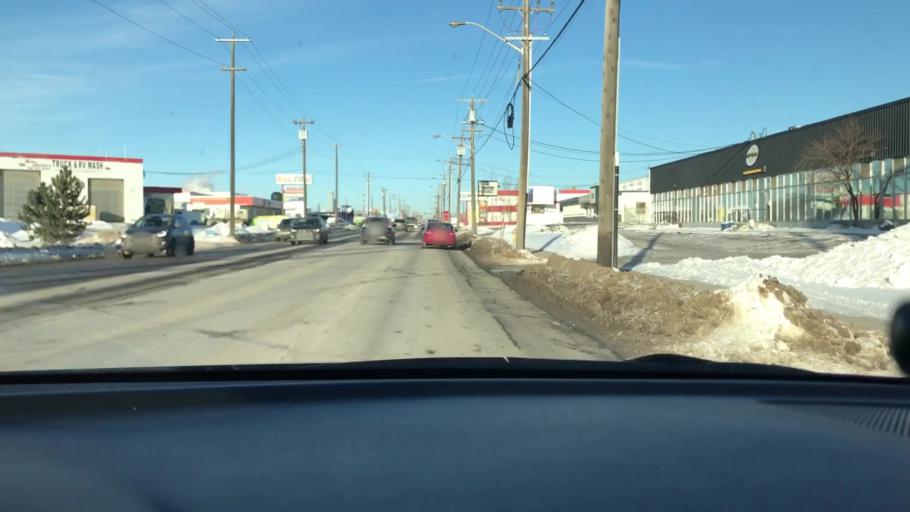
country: CA
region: Alberta
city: Edmonton
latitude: 53.4928
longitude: -113.4861
